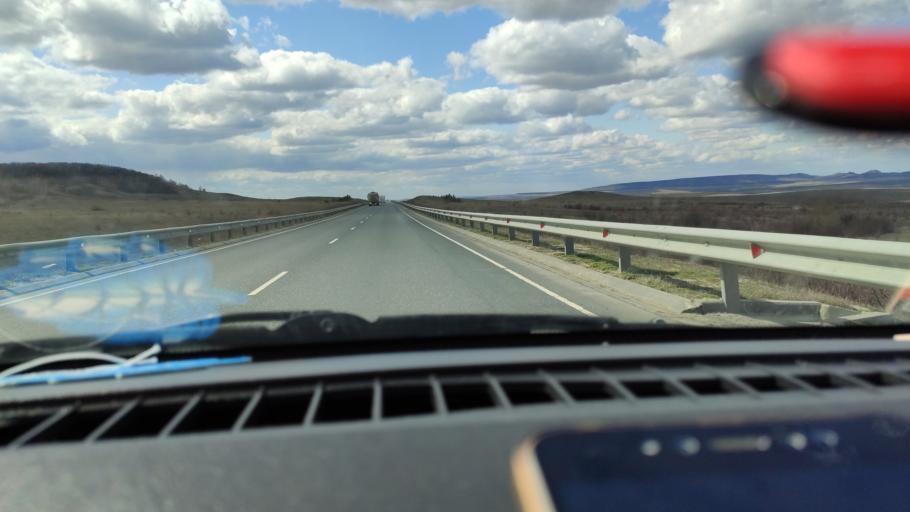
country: RU
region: Saratov
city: Alekseyevka
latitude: 52.3608
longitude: 47.9537
